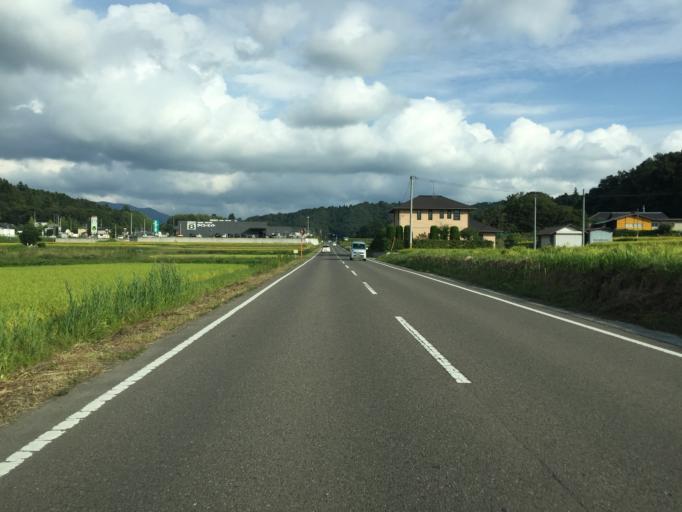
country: JP
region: Fukushima
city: Fukushima-shi
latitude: 37.6699
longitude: 140.5695
